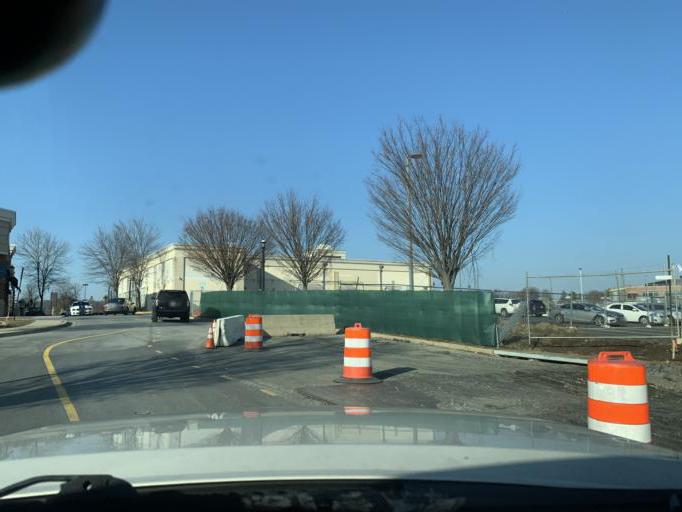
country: US
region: Maryland
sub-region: Prince George's County
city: Largo
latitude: 38.9006
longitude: -76.8469
